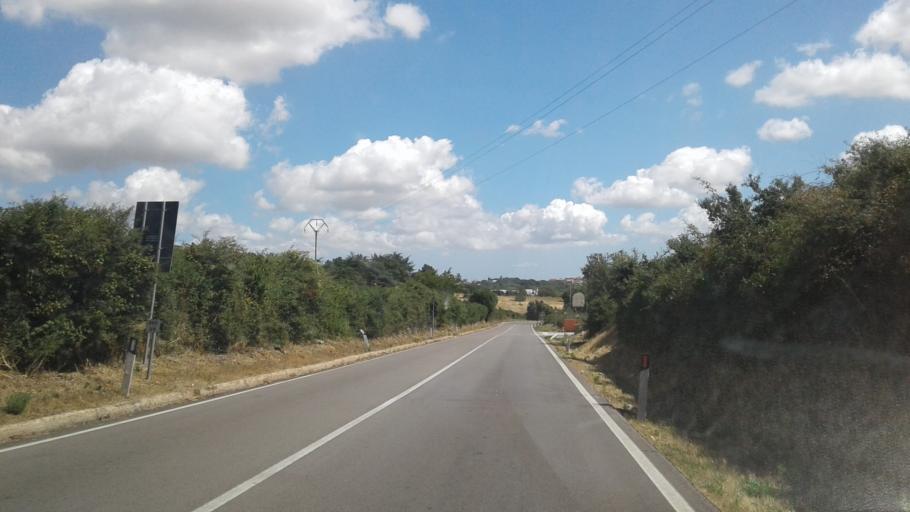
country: IT
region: Sardinia
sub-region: Provincia di Olbia-Tempio
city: Luras
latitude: 40.9092
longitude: 9.1560
